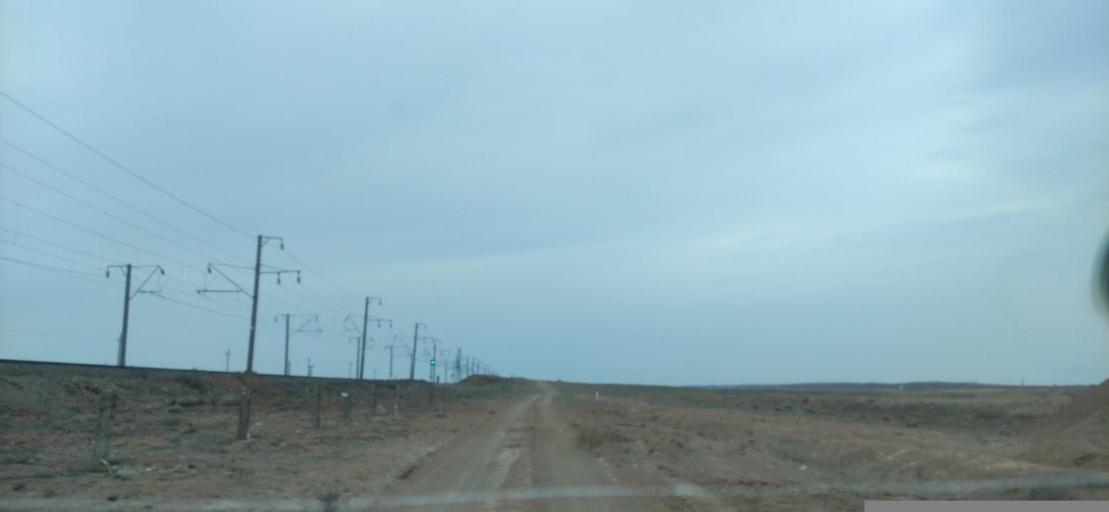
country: KZ
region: Qaraghandy
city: Saryshaghan
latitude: 46.1400
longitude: 73.6057
